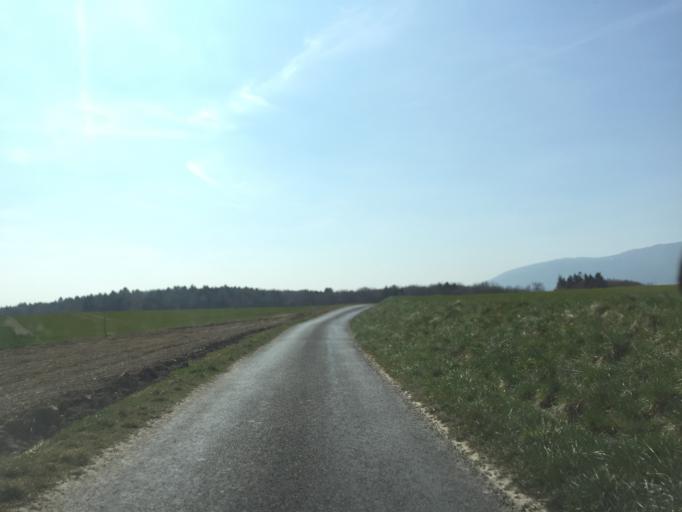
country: CH
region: Vaud
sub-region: Morges District
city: Chevilly
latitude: 46.6383
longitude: 6.4634
